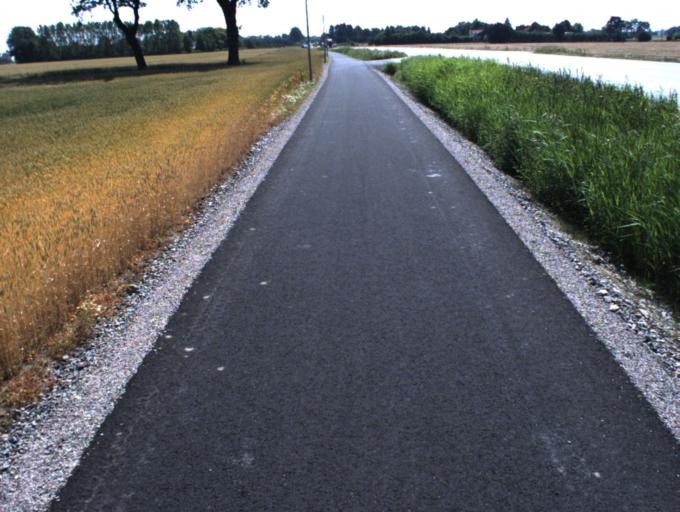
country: SE
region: Skane
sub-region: Helsingborg
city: Barslov
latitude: 56.0291
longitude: 12.7911
